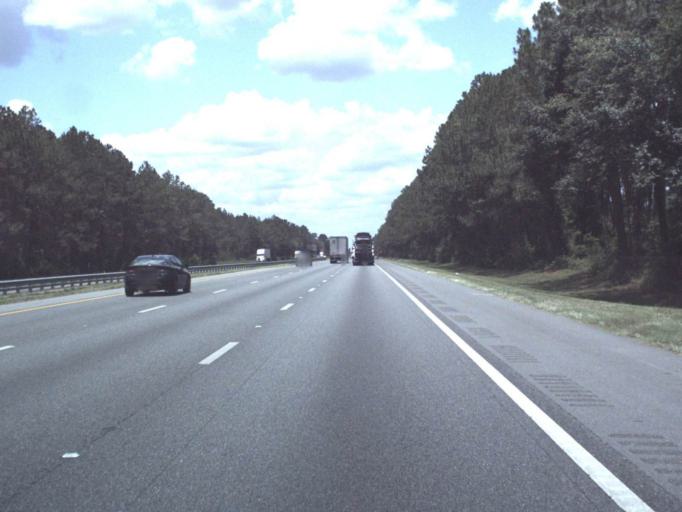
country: US
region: Florida
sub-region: Hamilton County
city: Jasper
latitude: 30.4605
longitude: -82.9521
